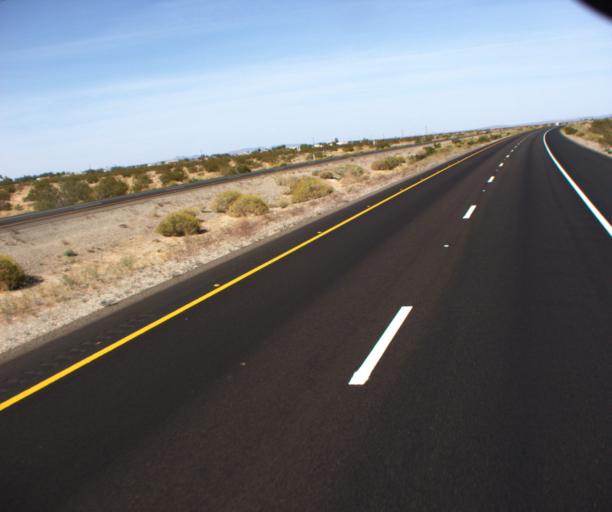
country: US
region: Arizona
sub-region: Yuma County
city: Fortuna Foothills
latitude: 32.5905
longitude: -114.5480
